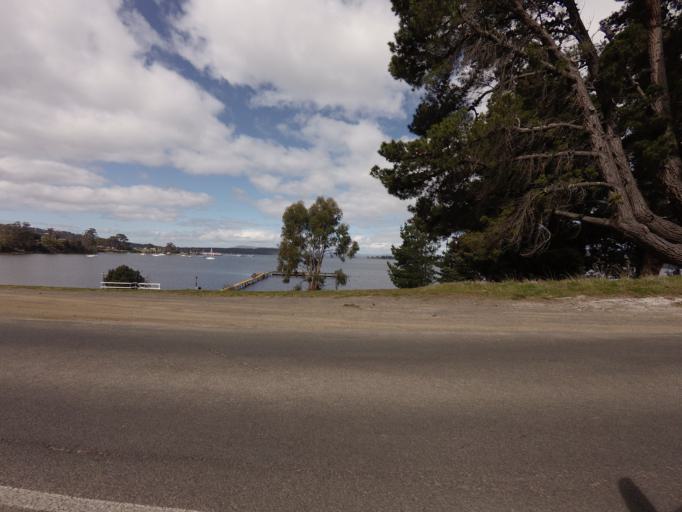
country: AU
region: Tasmania
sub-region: Huon Valley
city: Cygnet
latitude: -43.3176
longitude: 147.0105
